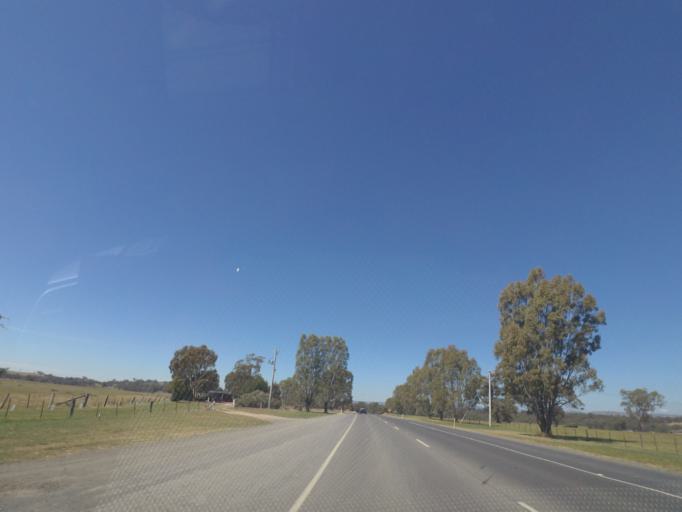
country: AU
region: Victoria
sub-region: Murrindindi
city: Kinglake West
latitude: -37.0297
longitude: 145.0856
